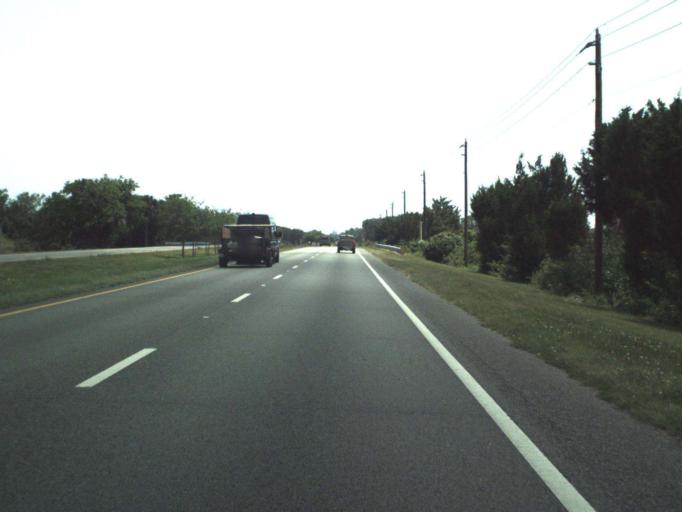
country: US
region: Florida
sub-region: Volusia County
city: Ormond Beach
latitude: 29.2968
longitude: -81.0812
